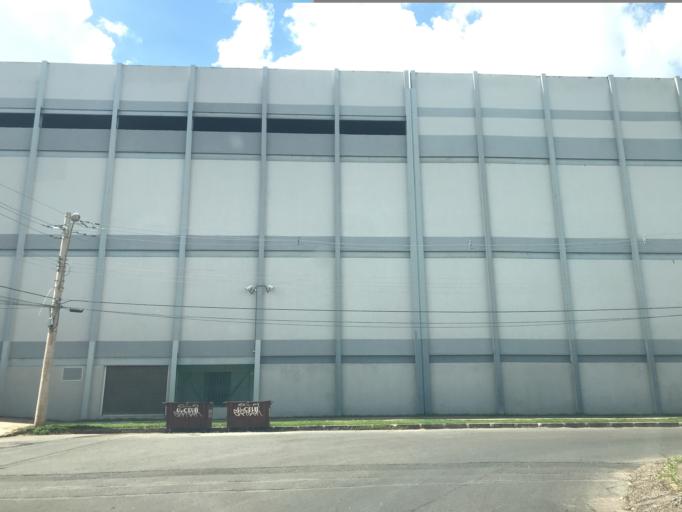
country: BR
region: Federal District
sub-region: Brasilia
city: Brasilia
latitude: -15.8369
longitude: -48.0456
